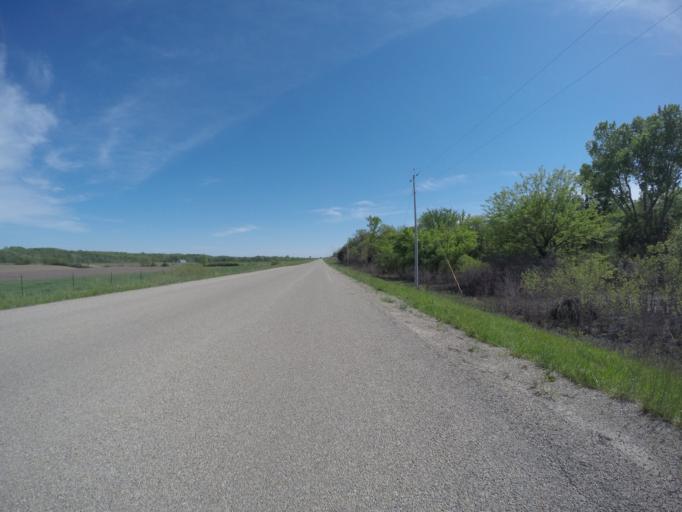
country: US
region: Kansas
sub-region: Riley County
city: Ogden
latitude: 39.0204
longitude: -96.6075
